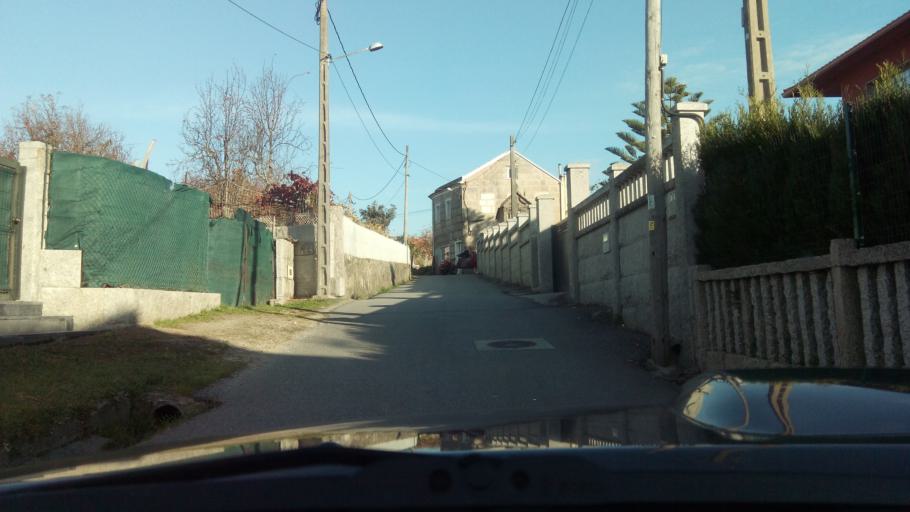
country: ES
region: Galicia
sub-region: Provincia de Pontevedra
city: Marin
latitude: 42.3638
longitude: -8.7028
